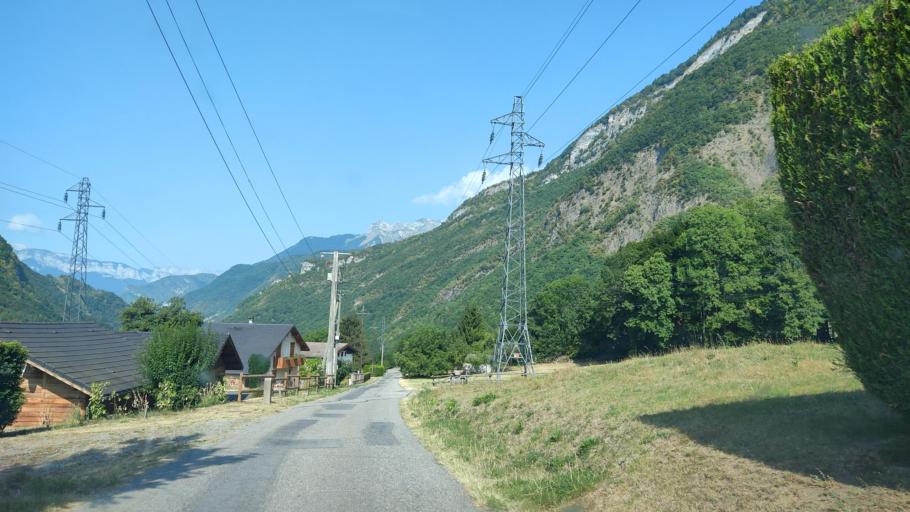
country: FR
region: Rhone-Alpes
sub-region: Departement de la Savoie
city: Ugine
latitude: 45.7662
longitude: 6.3917
